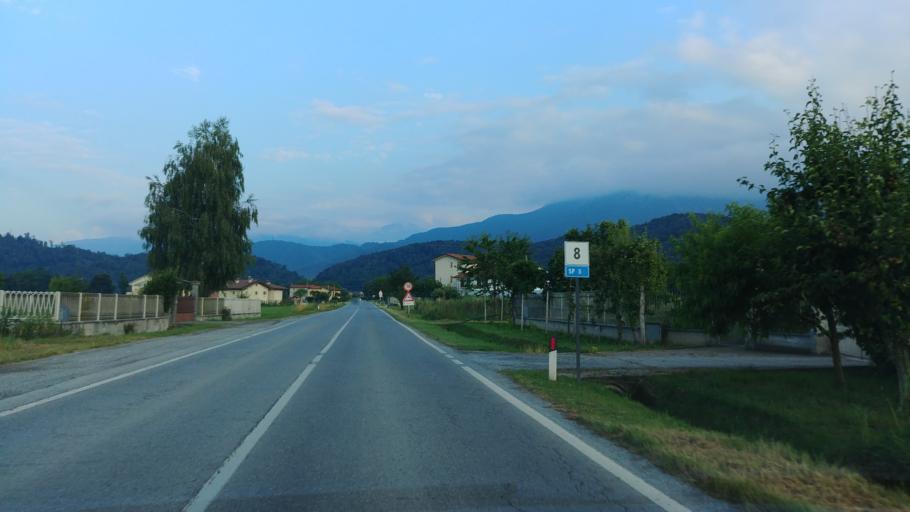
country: IT
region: Piedmont
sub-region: Provincia di Cuneo
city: Peveragno
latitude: 44.3437
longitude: 7.5968
